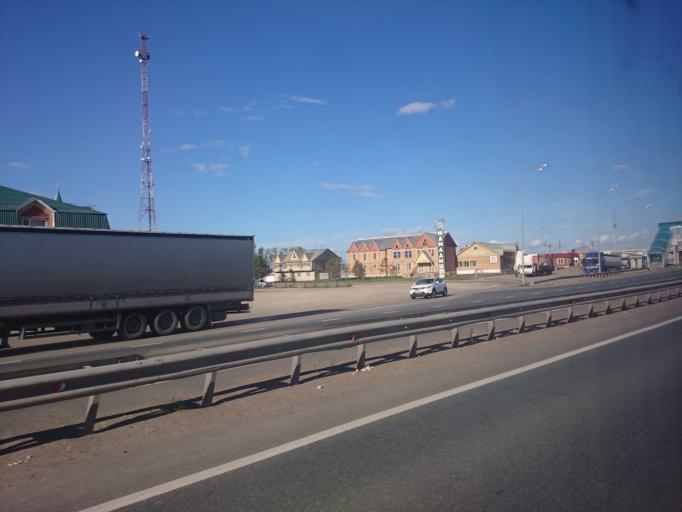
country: RU
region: Tatarstan
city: Mamadysh
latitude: 55.6489
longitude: 51.3834
